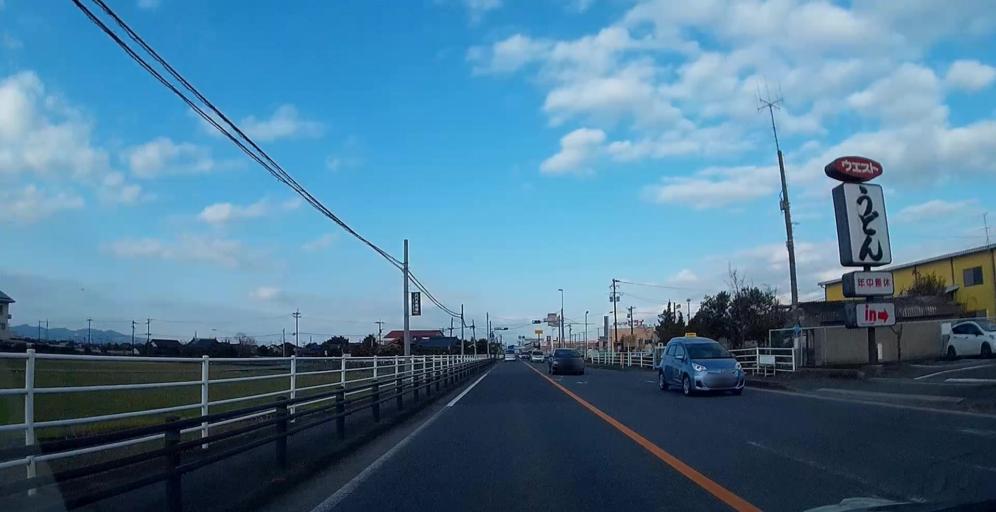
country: JP
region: Kumamoto
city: Yatsushiro
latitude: 32.5505
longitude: 130.6787
